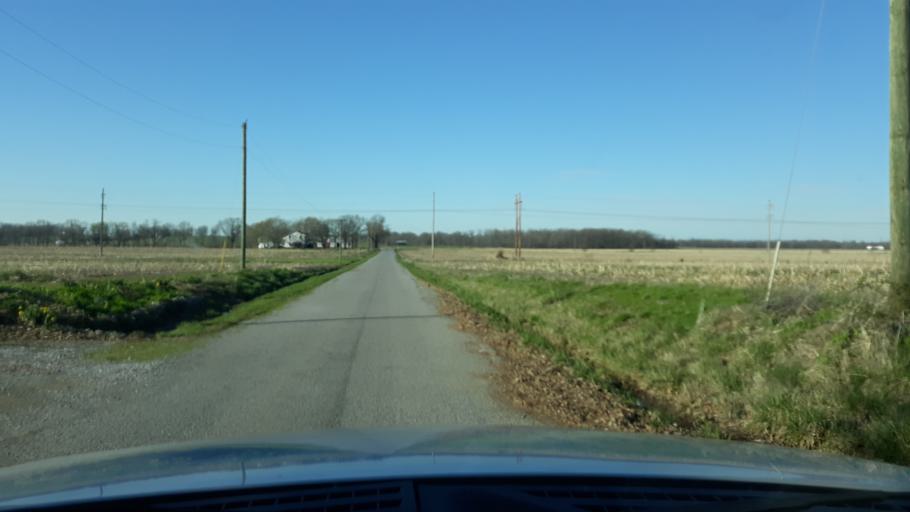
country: US
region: Illinois
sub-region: Saline County
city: Harrisburg
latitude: 37.7666
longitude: -88.5864
